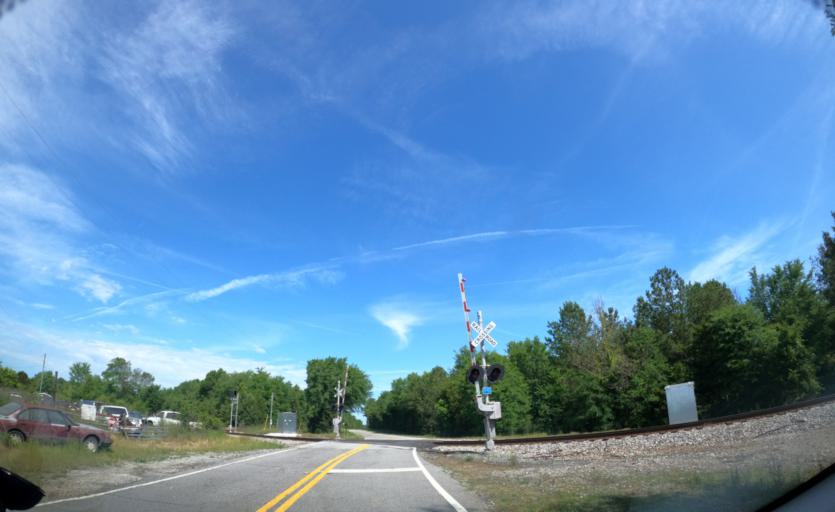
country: US
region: South Carolina
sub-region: Abbeville County
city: Calhoun Falls
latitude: 34.1086
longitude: -82.7238
